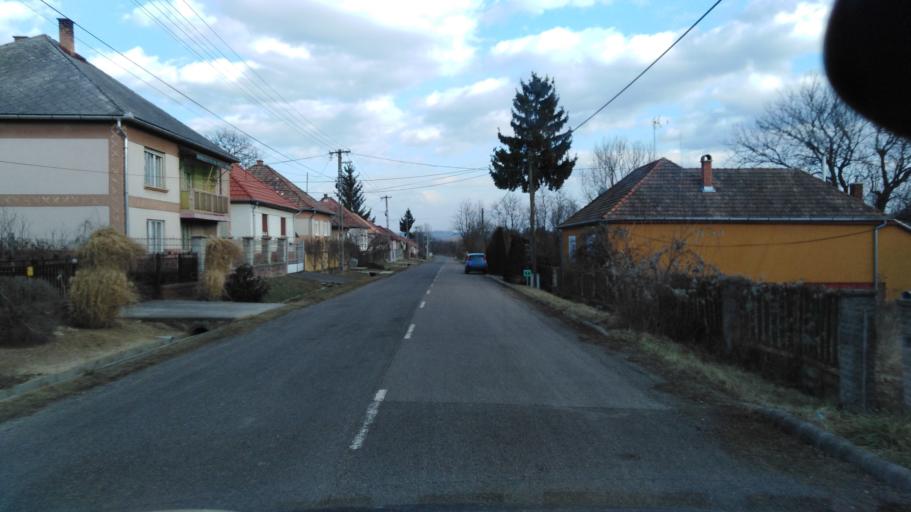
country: HU
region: Nograd
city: Matranovak
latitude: 48.1491
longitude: 19.9543
